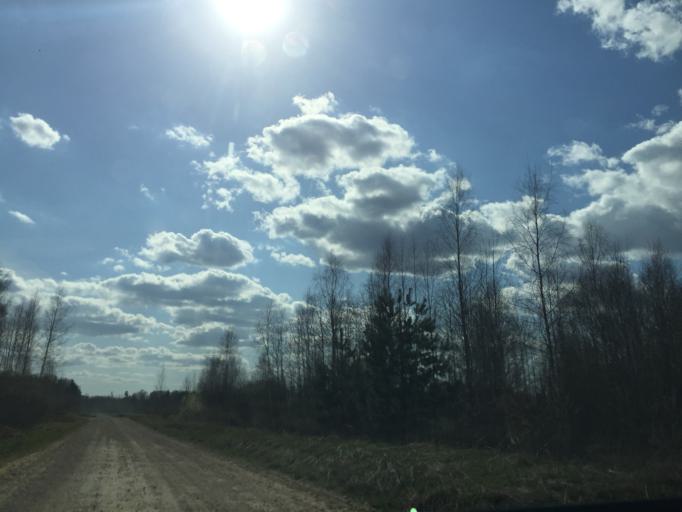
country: LV
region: Skriveri
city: Skriveri
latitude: 56.7655
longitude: 25.1834
